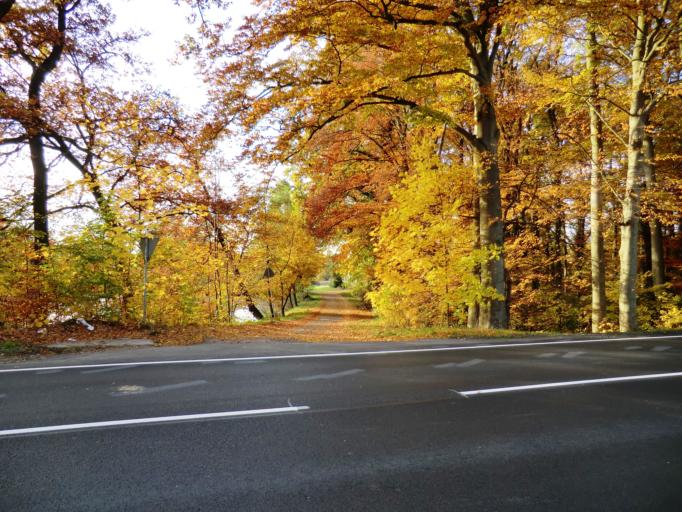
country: DE
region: North Rhine-Westphalia
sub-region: Regierungsbezirk Detmold
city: Herford
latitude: 52.1431
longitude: 8.6493
